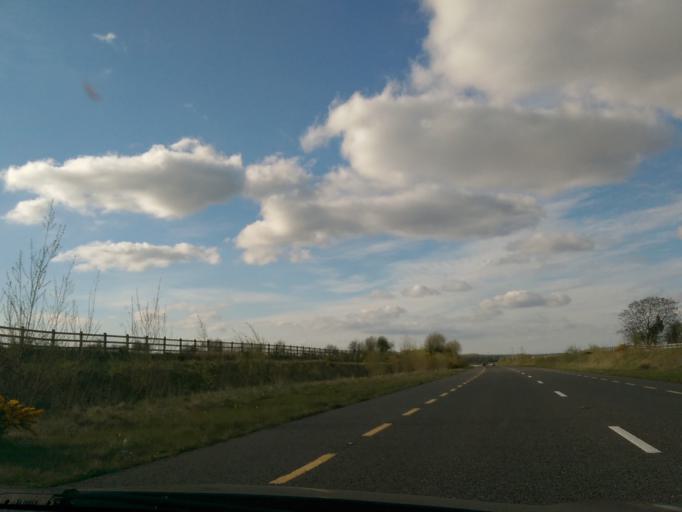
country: IE
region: Connaught
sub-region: County Galway
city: Loughrea
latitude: 53.2486
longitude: -8.5944
